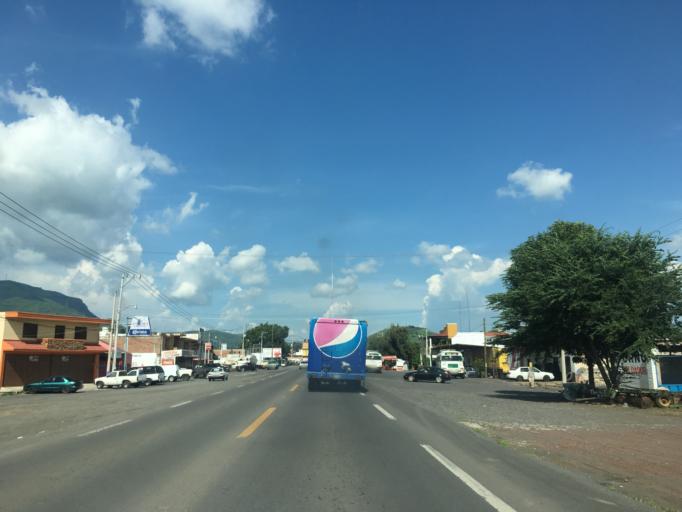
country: MX
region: Nayarit
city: Ixtlan del Rio
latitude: 21.0377
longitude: -104.3827
